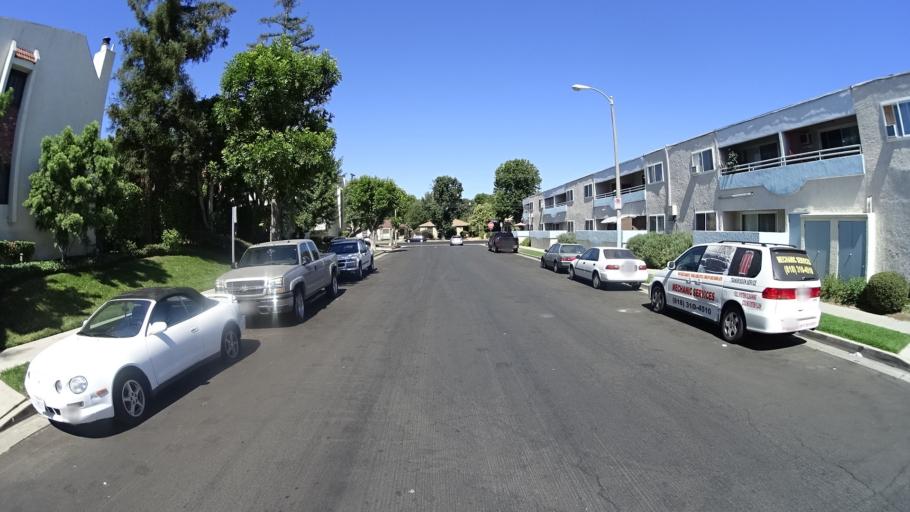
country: US
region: California
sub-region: Los Angeles County
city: Van Nuys
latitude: 34.1903
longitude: -118.4916
